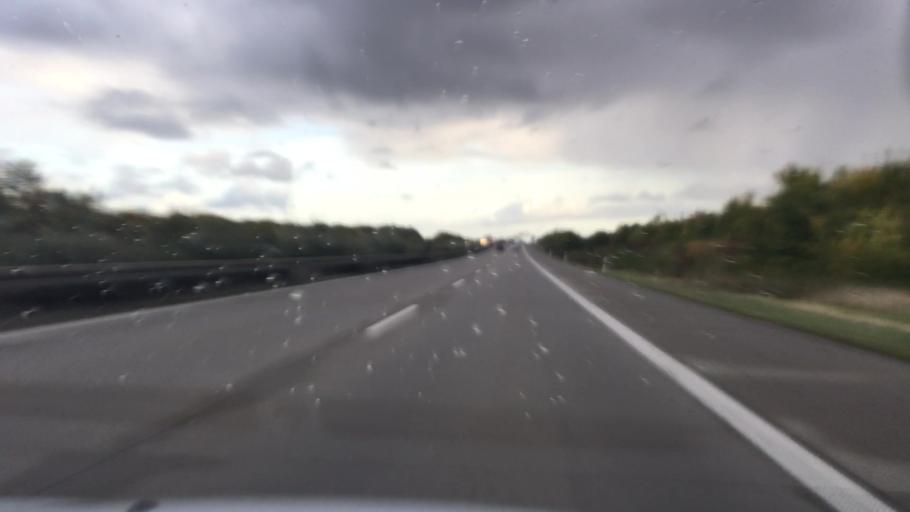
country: DE
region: Saxony-Anhalt
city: Welsleben
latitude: 52.0176
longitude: 11.6500
